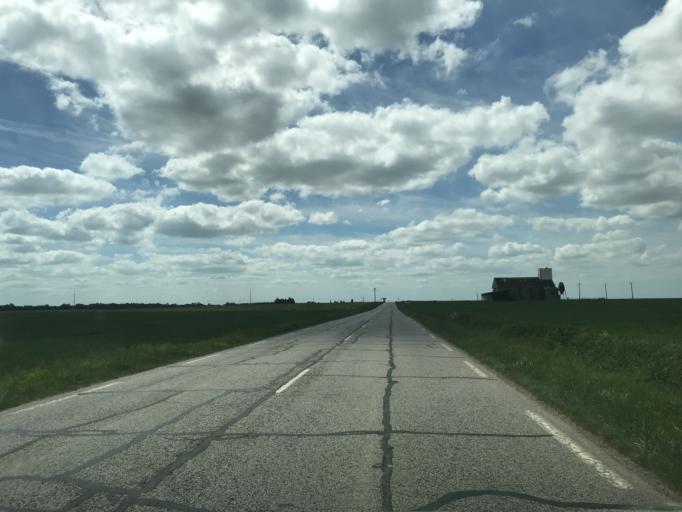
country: FR
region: Haute-Normandie
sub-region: Departement de l'Eure
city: La Haye-Malherbe
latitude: 49.1800
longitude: 1.0635
